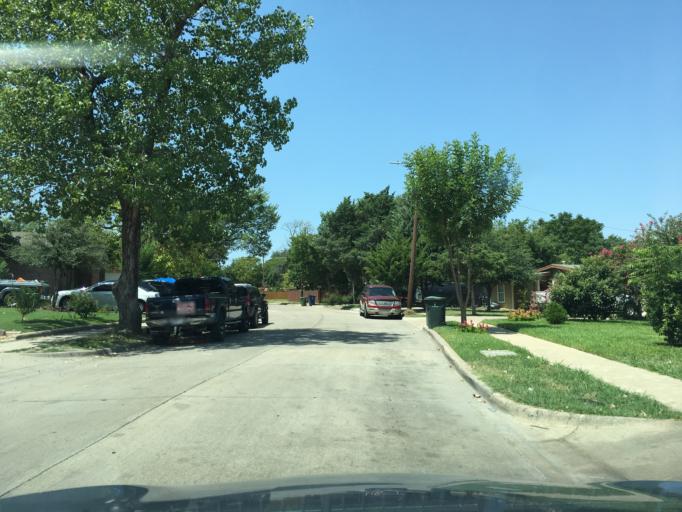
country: US
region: Texas
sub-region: Dallas County
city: Garland
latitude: 32.8959
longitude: -96.6249
